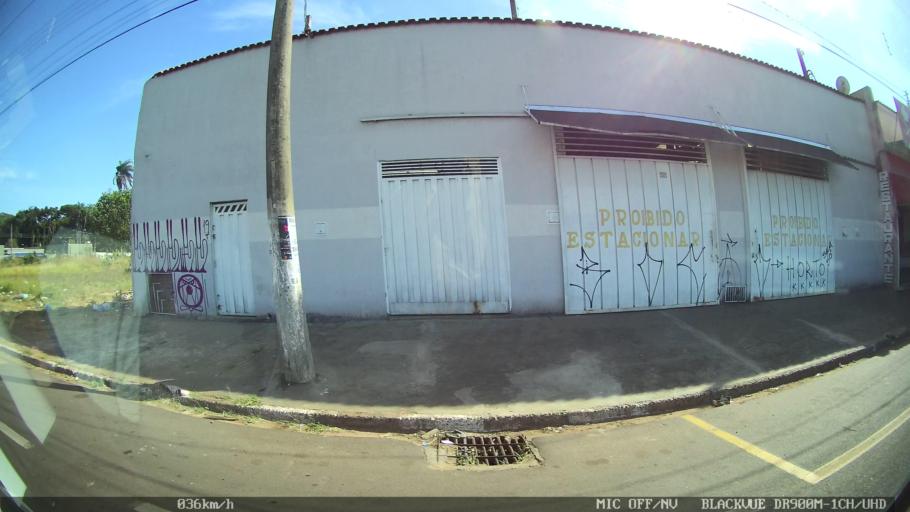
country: BR
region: Sao Paulo
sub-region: Franca
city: Franca
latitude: -20.4892
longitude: -47.3988
